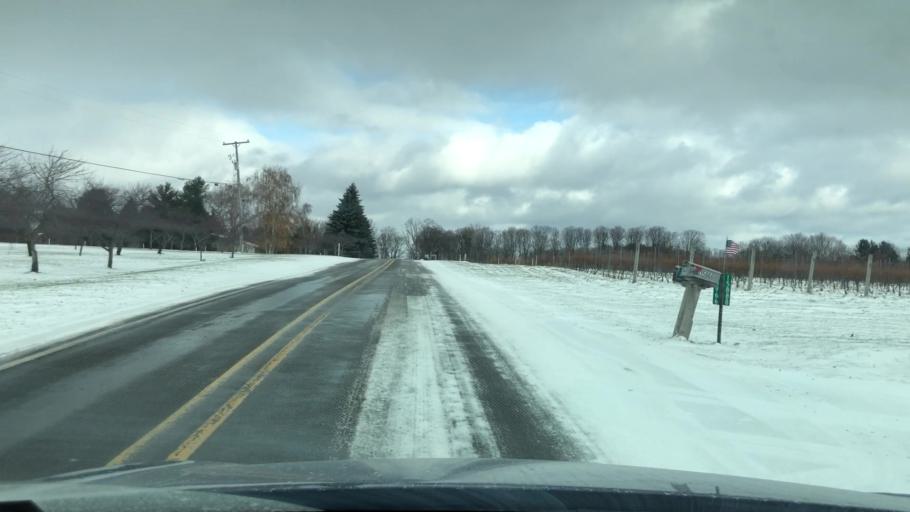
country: US
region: Michigan
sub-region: Antrim County
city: Elk Rapids
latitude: 44.9214
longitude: -85.4983
